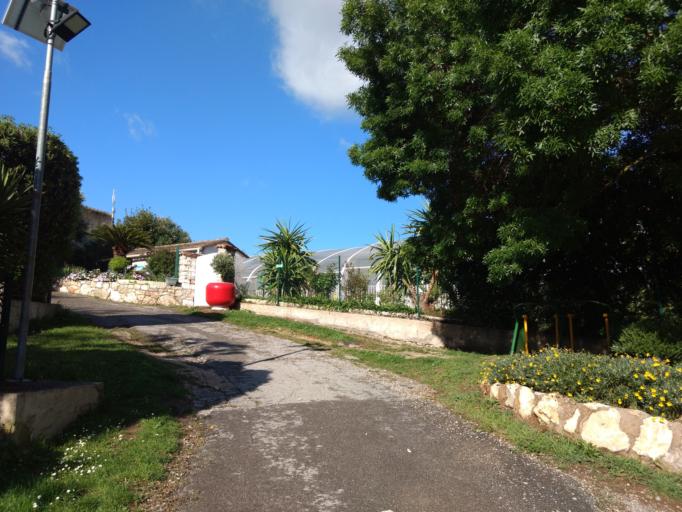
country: FR
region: Provence-Alpes-Cote d'Azur
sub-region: Departement des Alpes-Maritimes
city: Biot
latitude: 43.6207
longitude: 7.1259
